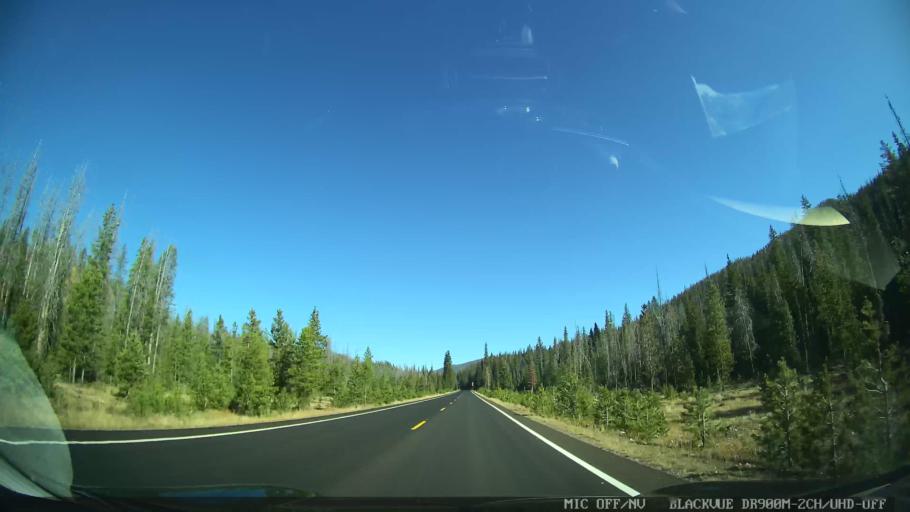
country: US
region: Colorado
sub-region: Grand County
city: Granby
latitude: 40.2931
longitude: -105.8428
